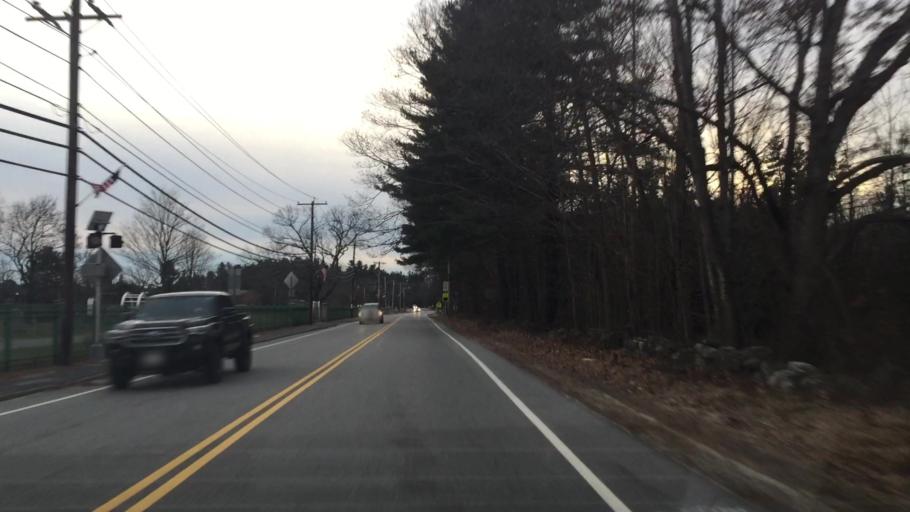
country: US
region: New Hampshire
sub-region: Hillsborough County
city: Pelham
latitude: 42.7303
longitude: -71.3257
